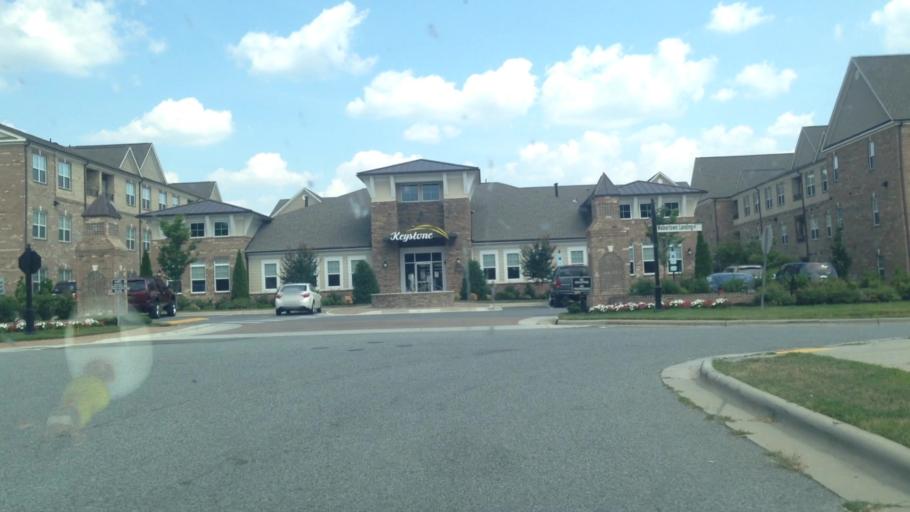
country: US
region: North Carolina
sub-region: Forsyth County
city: Walkertown
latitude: 36.1665
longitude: -80.1344
